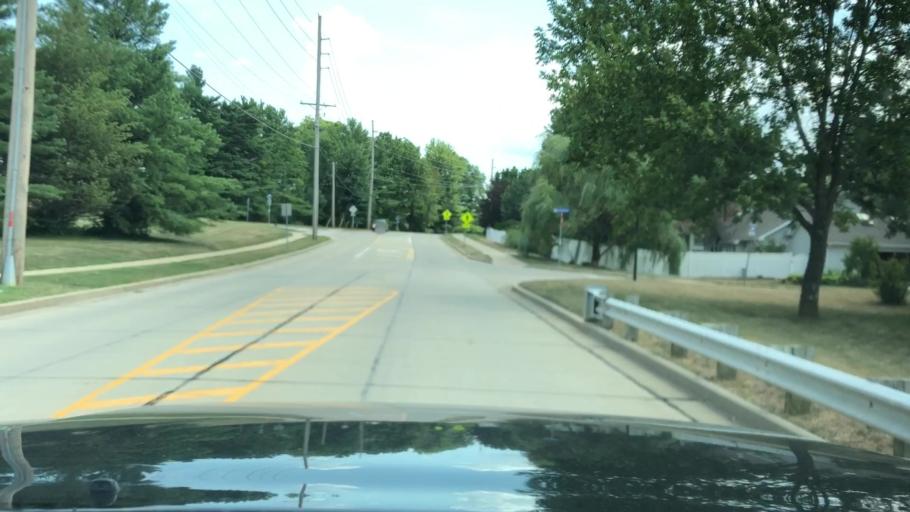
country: US
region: Missouri
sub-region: Saint Charles County
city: Saint Charles
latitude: 38.8071
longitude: -90.5363
